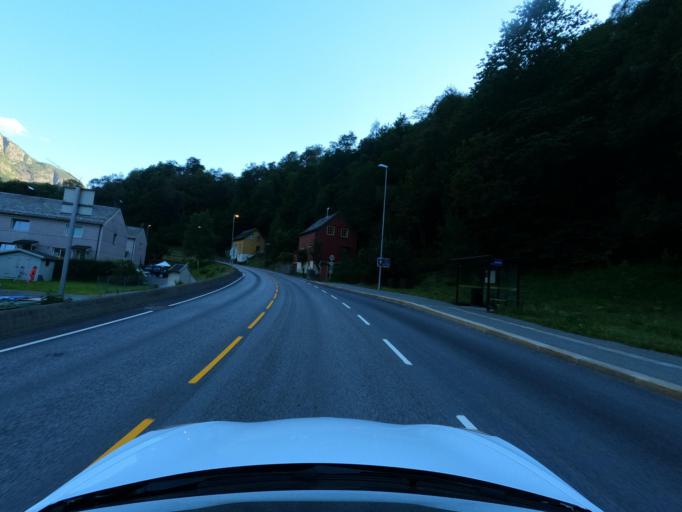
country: NO
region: Hordaland
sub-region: Odda
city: Odda
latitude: 60.0589
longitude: 6.5476
